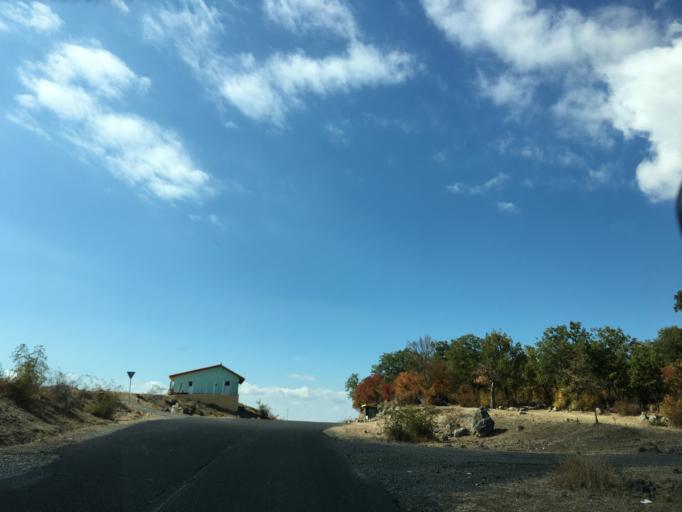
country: BG
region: Kurdzhali
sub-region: Obshtina Kurdzhali
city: Kurdzhali
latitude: 41.5317
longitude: 25.4745
